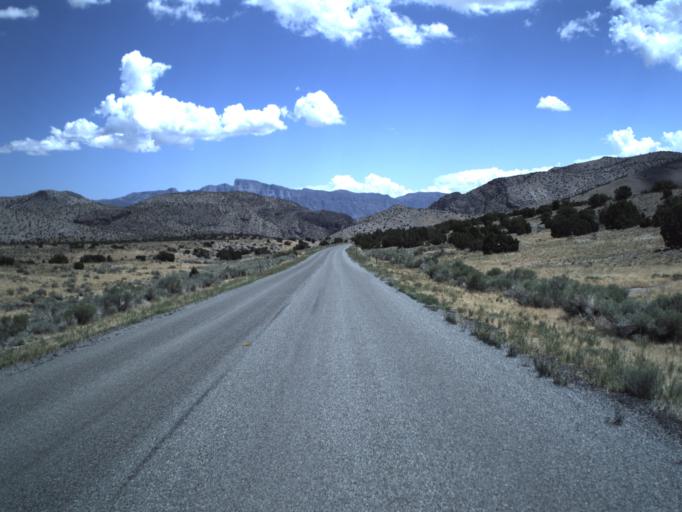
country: US
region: Utah
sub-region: Beaver County
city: Milford
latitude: 39.0755
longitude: -113.6324
